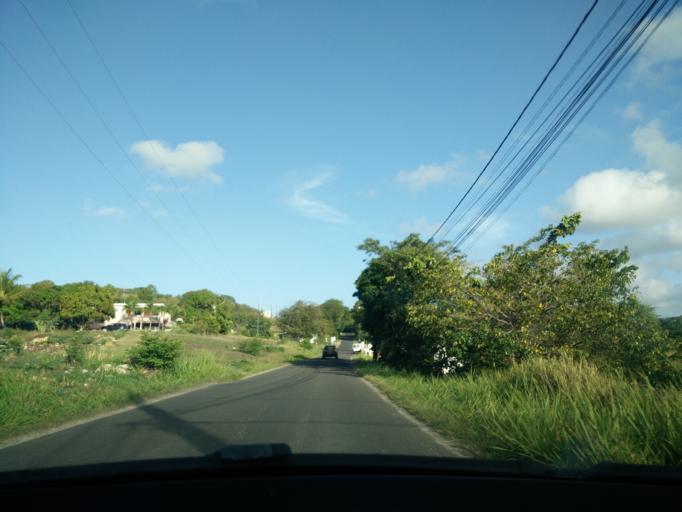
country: GP
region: Guadeloupe
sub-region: Guadeloupe
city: Sainte-Anne
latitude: 16.2764
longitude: -61.3905
